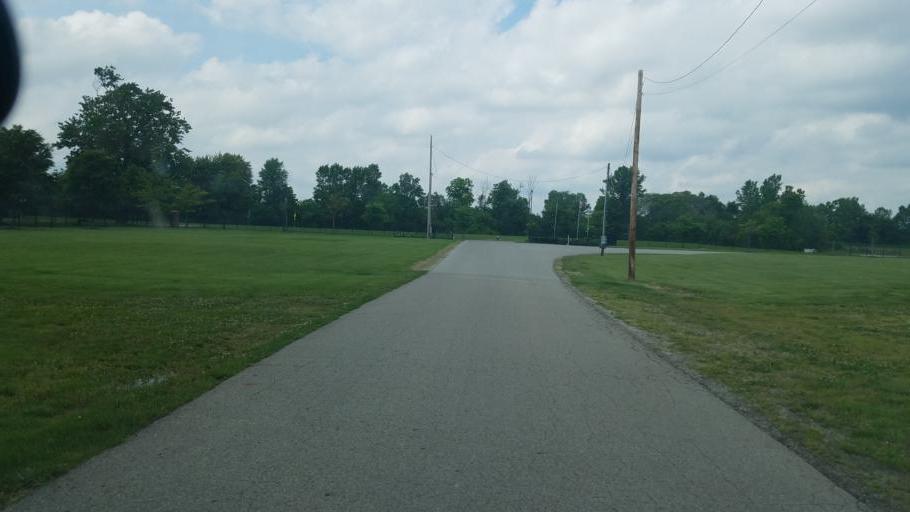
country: US
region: Ohio
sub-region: Franklin County
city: Hilliard
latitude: 40.0368
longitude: -83.1533
